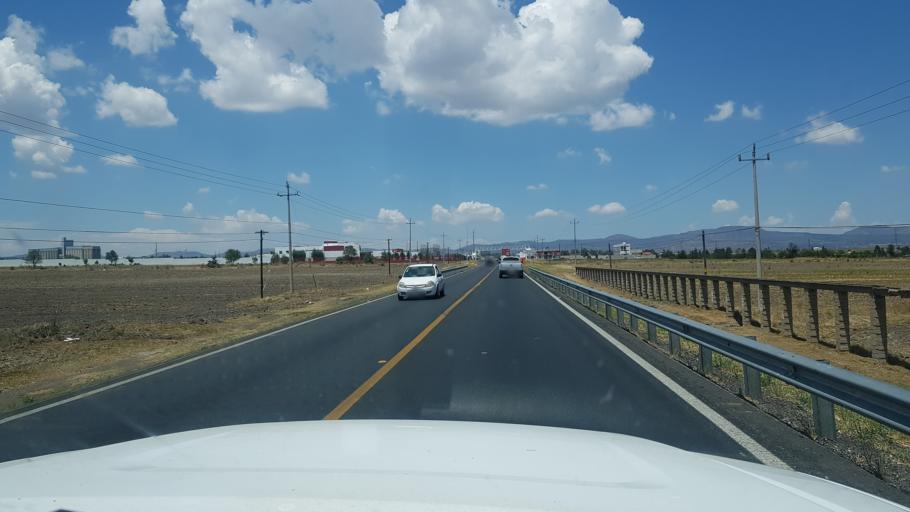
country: MX
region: Hidalgo
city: Calpulalpan
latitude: 19.5819
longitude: -98.5328
